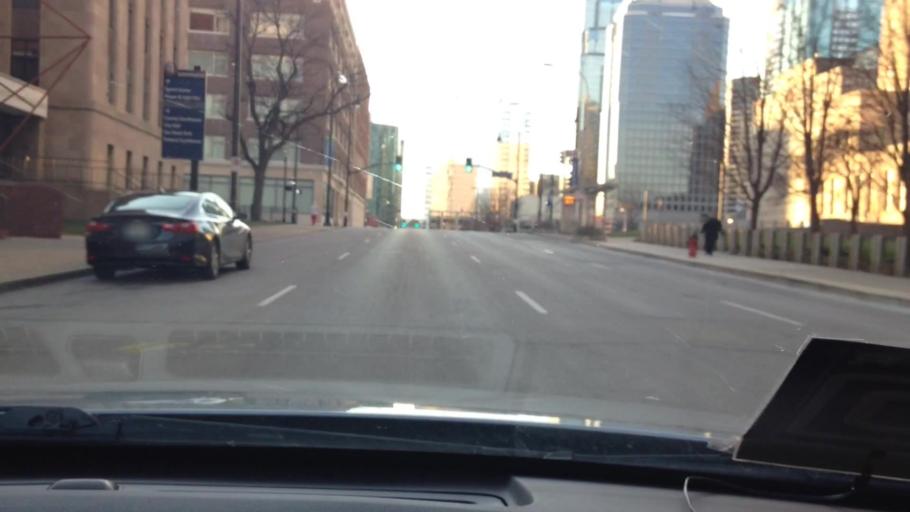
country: US
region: Missouri
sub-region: Jackson County
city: Kansas City
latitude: 39.0984
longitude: -94.5766
